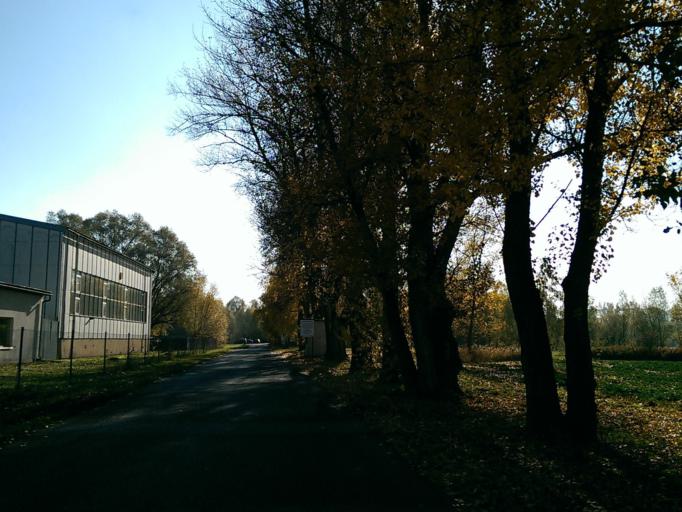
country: CZ
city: Prisovice
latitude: 50.5691
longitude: 15.0840
